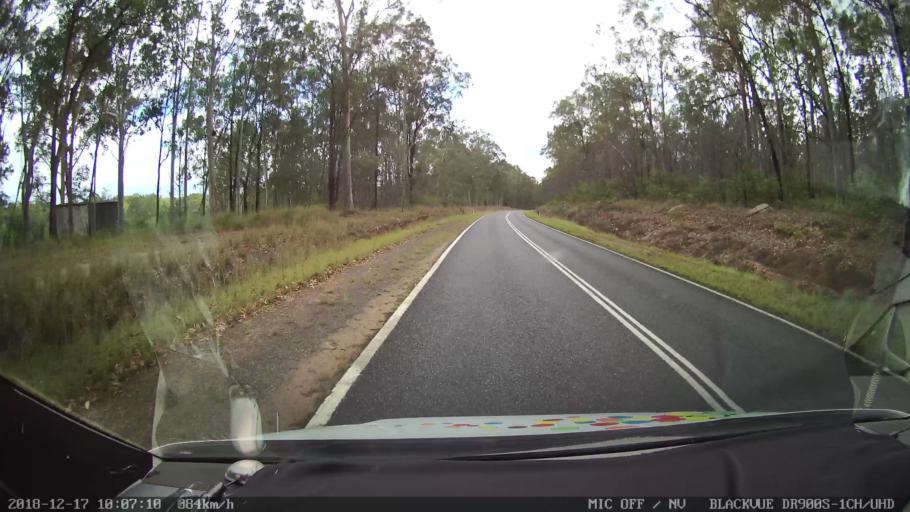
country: AU
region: New South Wales
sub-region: Tenterfield Municipality
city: Carrolls Creek
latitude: -28.8888
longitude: 152.5145
